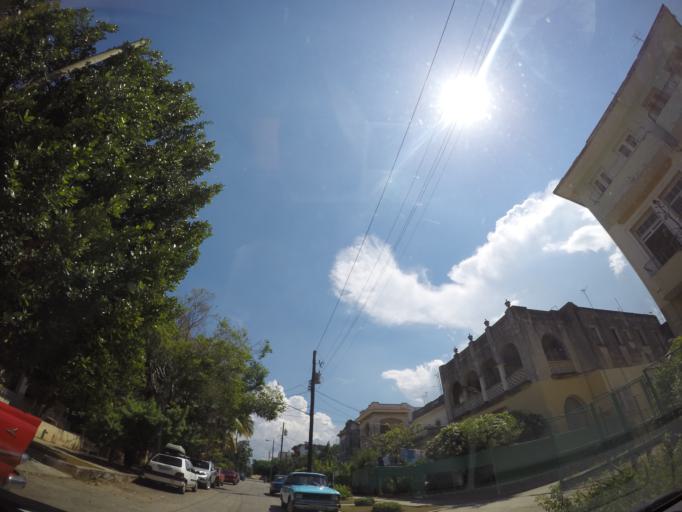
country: CU
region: La Habana
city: Havana
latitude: 23.1262
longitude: -82.4046
